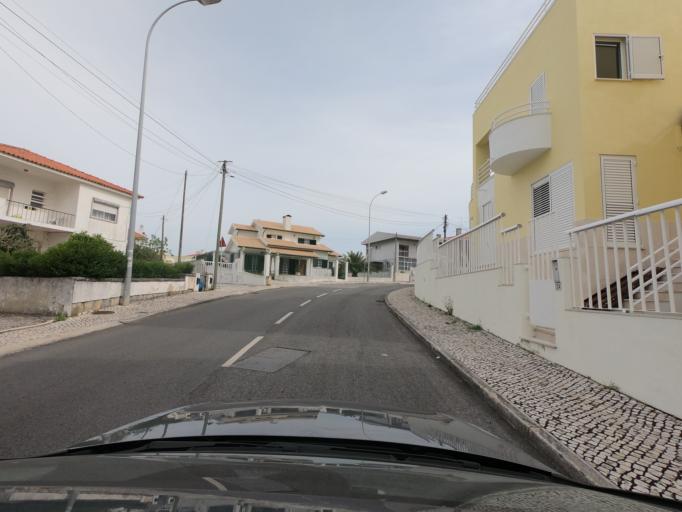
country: PT
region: Lisbon
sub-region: Oeiras
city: Porto Salvo
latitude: 38.7186
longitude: -9.2983
